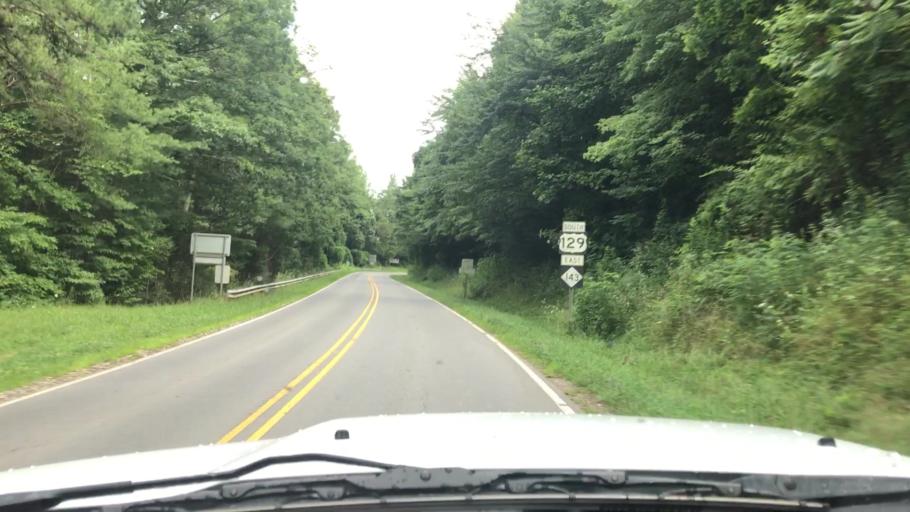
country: US
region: North Carolina
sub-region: Graham County
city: Robbinsville
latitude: 35.3395
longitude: -83.8137
